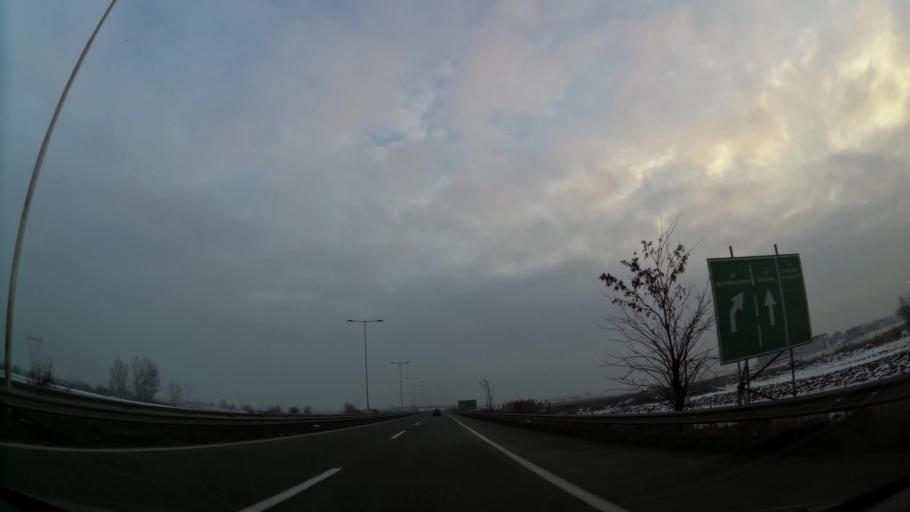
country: MK
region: Aracinovo
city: Arachinovo
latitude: 42.0134
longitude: 21.5344
